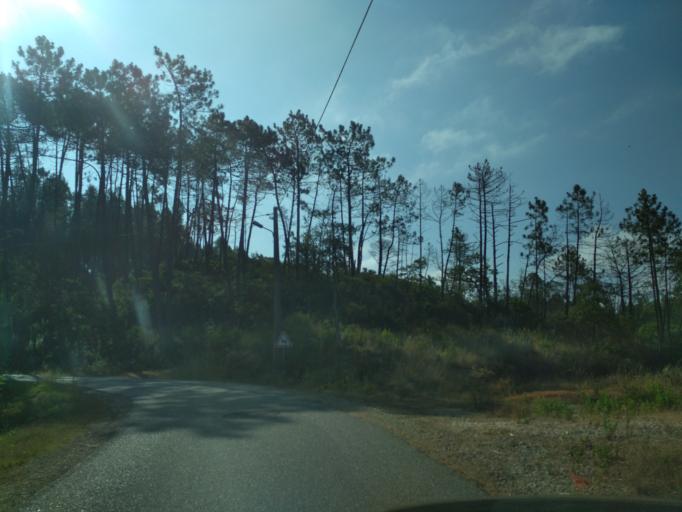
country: PT
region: Coimbra
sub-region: Soure
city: Soure
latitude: 39.9933
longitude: -8.5772
